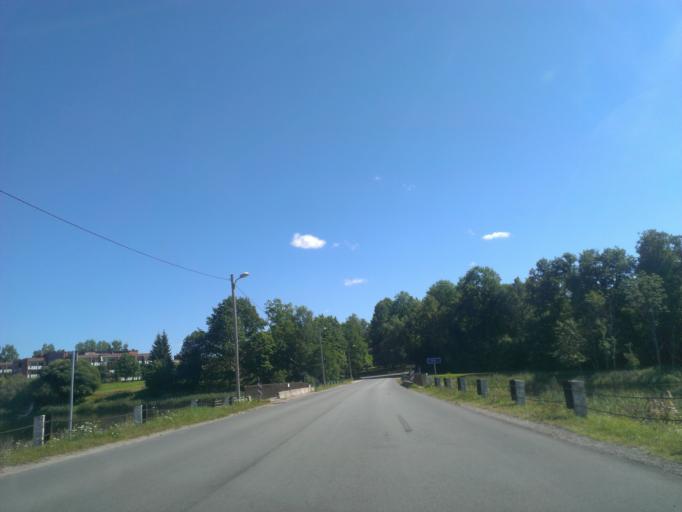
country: LV
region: Malpils
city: Malpils
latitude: 57.0108
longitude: 24.9470
